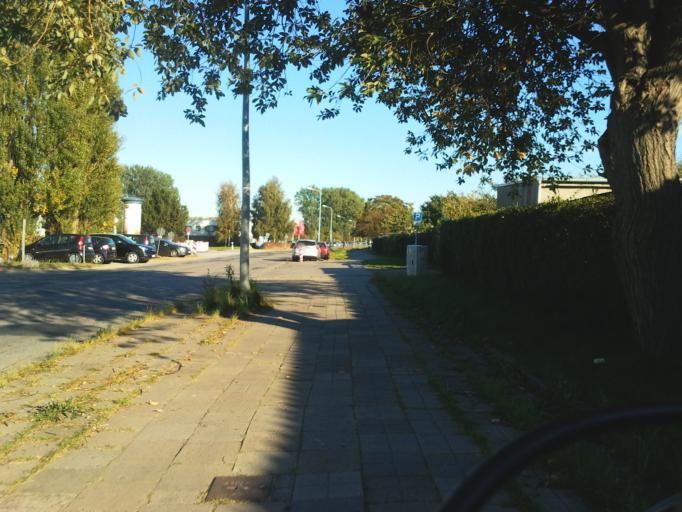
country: DE
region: Mecklenburg-Vorpommern
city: Lambrechtshagen
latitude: 54.1138
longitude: 12.0701
